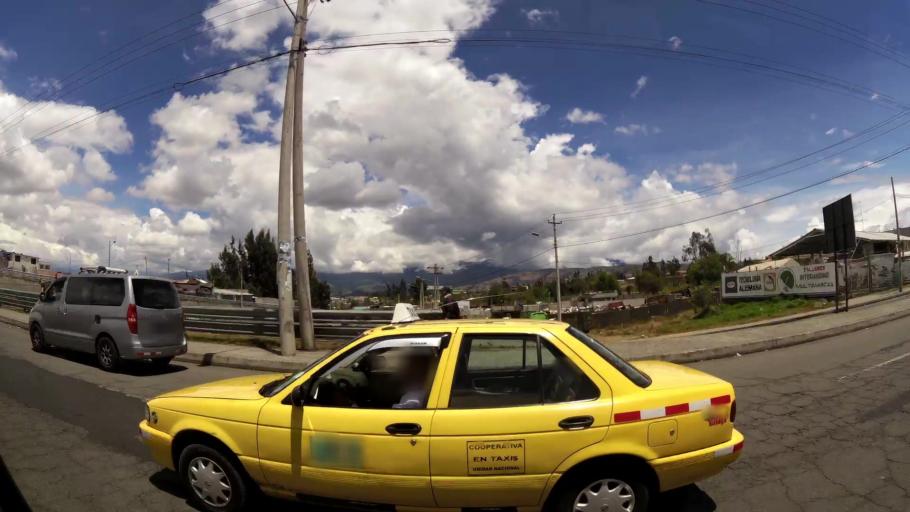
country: EC
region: Tungurahua
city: Ambato
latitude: -1.2725
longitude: -78.6114
